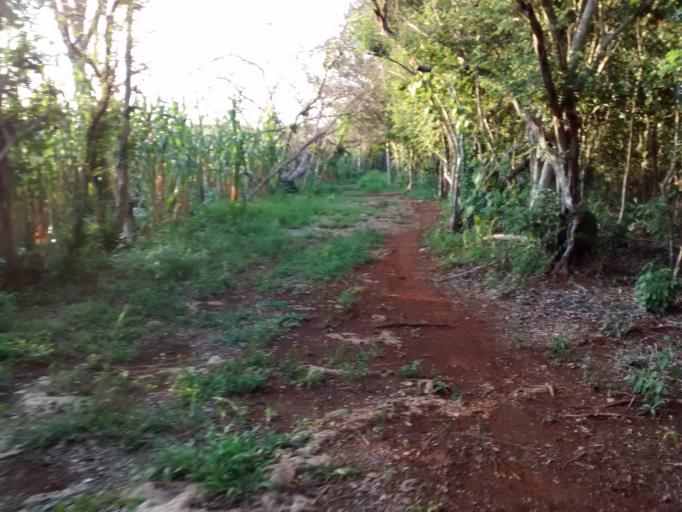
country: MX
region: Yucatan
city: Valladolid
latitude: 20.6572
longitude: -88.1842
